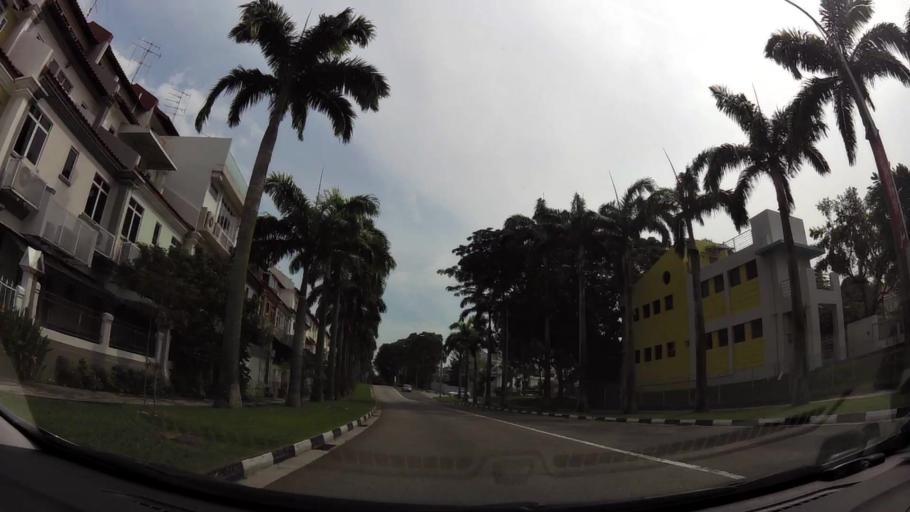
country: SG
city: Singapore
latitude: 1.3622
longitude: 103.9654
